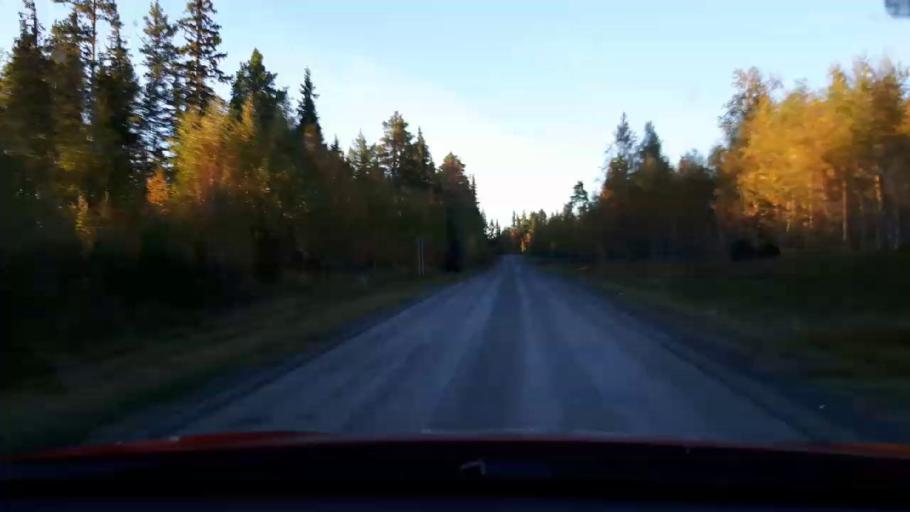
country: SE
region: Jaemtland
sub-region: Krokoms Kommun
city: Krokom
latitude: 63.4415
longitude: 14.4217
